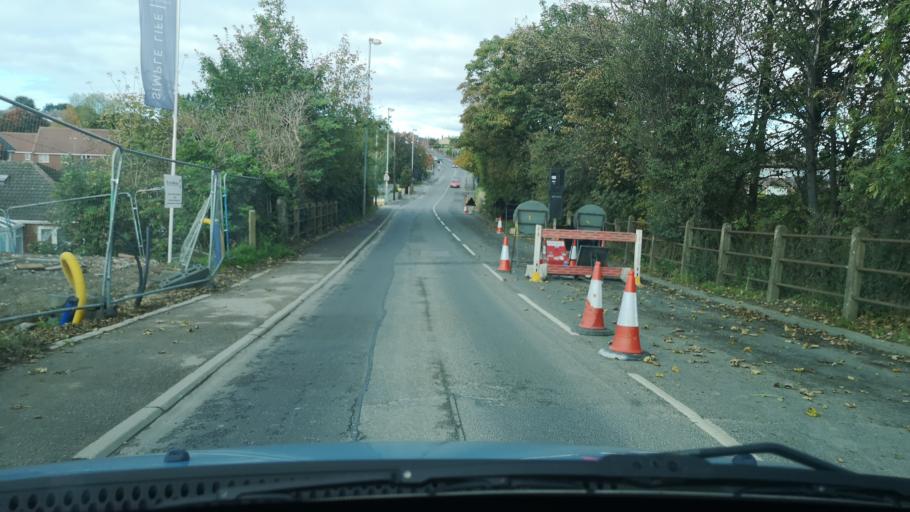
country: GB
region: England
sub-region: City and Borough of Wakefield
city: Normanton
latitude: 53.7025
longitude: -1.4240
